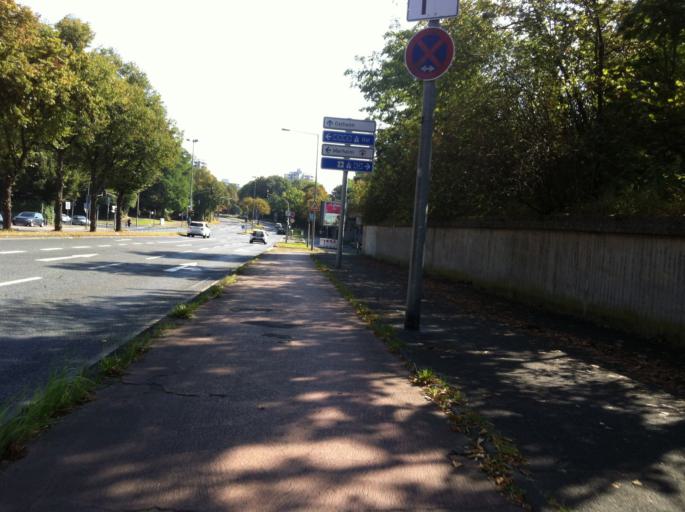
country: DE
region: North Rhine-Westphalia
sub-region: Regierungsbezirk Koln
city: Hoehenberg
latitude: 50.9317
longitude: 7.0290
